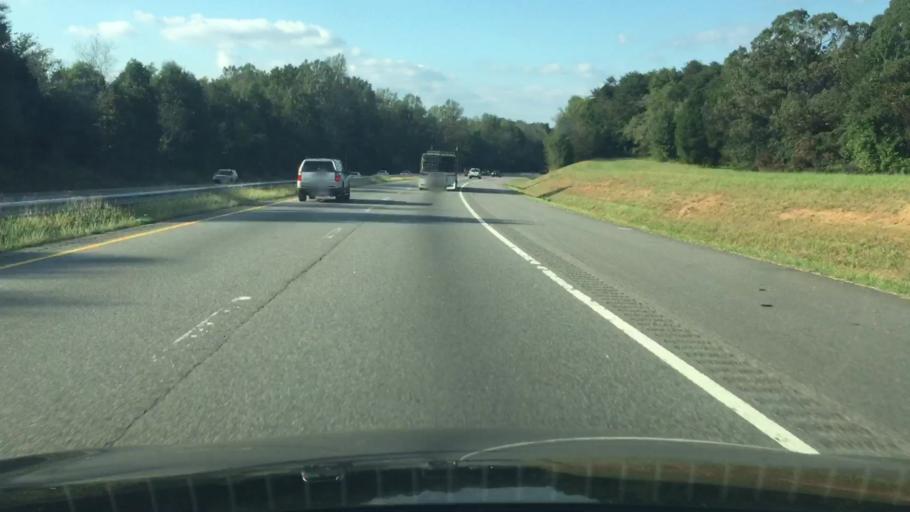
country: US
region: North Carolina
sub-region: Iredell County
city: Troutman
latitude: 35.6959
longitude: -80.8578
